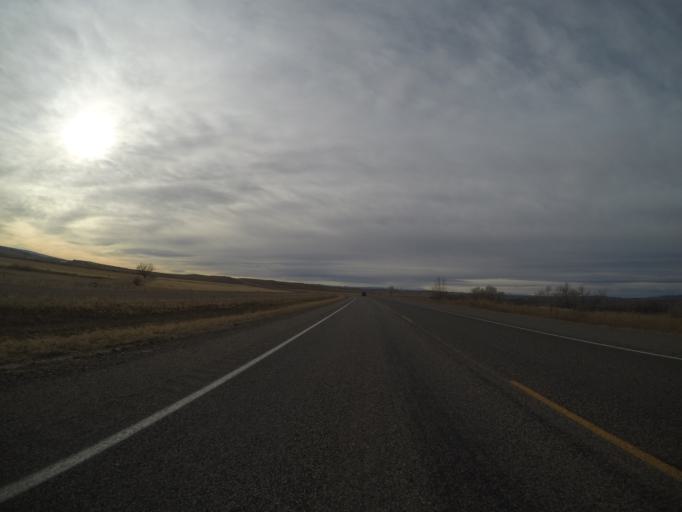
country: US
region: Montana
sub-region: Yellowstone County
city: Laurel
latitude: 45.6149
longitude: -108.8181
